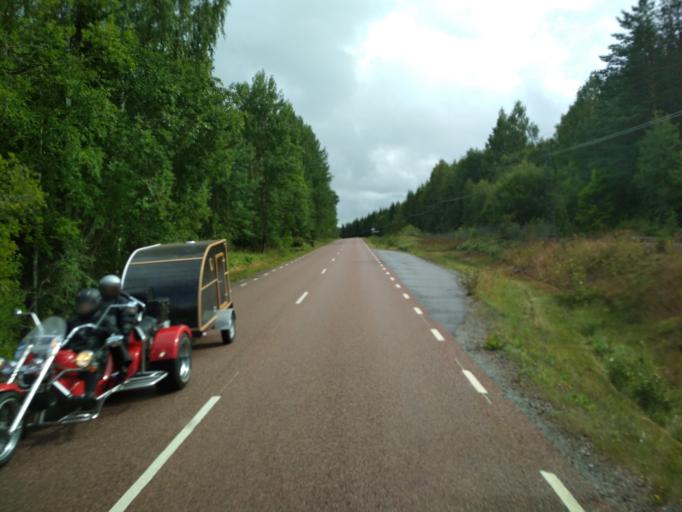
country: SE
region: Vaestmanland
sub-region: Surahammars Kommun
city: Ramnas
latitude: 59.8085
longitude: 16.1666
